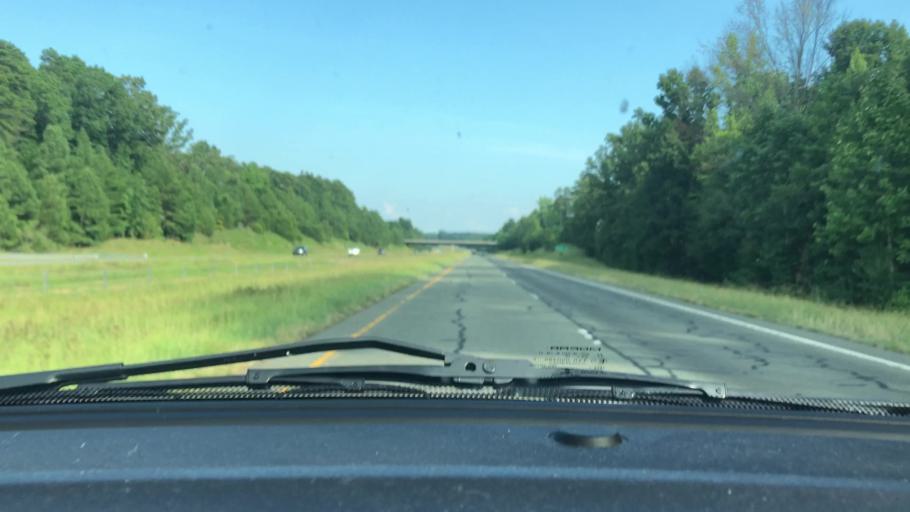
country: US
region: North Carolina
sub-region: Randolph County
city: Liberty
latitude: 35.8009
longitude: -79.5386
